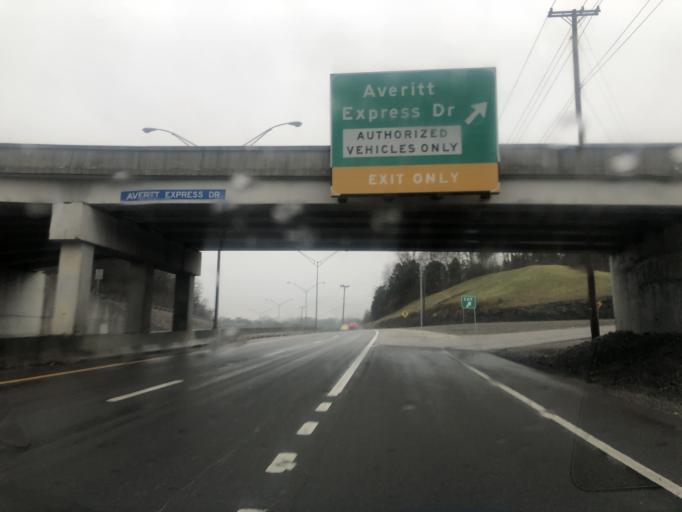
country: US
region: Tennessee
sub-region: Davidson County
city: Oak Hill
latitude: 36.1105
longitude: -86.7168
